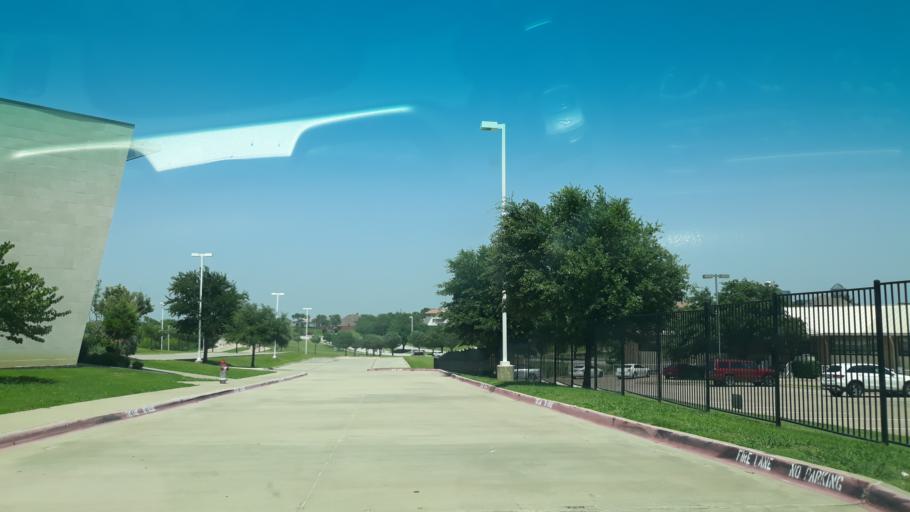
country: US
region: Texas
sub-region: Dallas County
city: Irving
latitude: 32.8671
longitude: -96.9617
